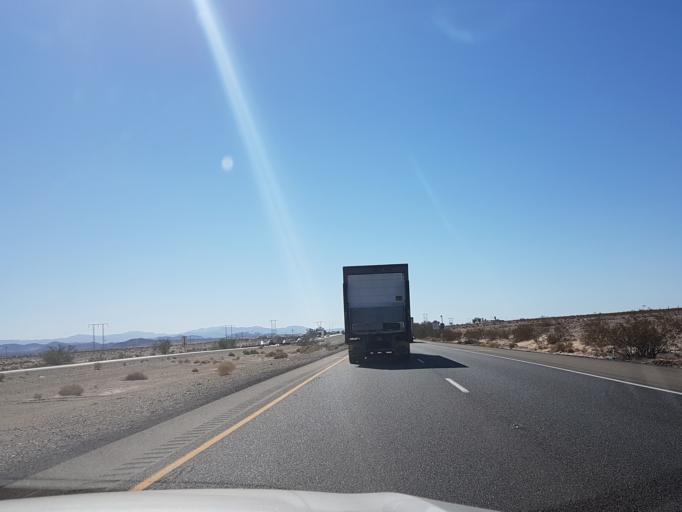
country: US
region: California
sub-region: San Bernardino County
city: Fort Irwin
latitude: 35.0390
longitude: -116.4615
